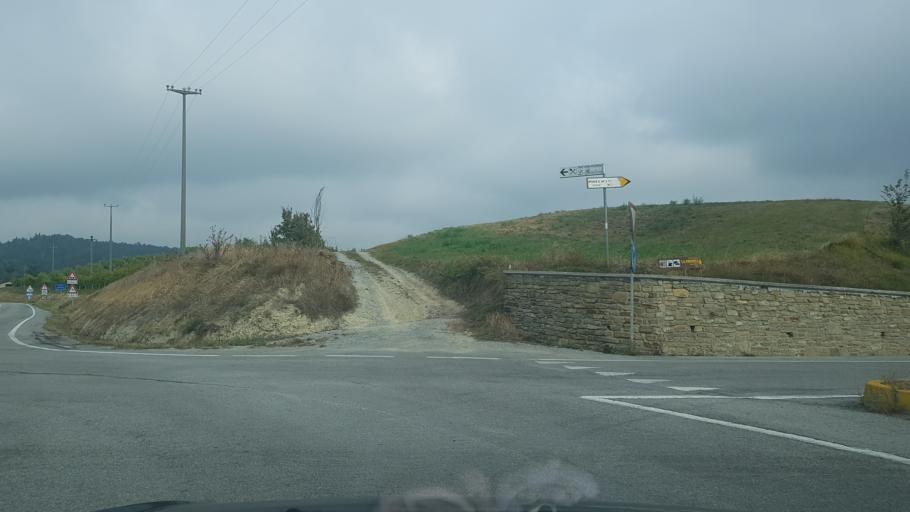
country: IT
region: Piedmont
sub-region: Provincia di Cuneo
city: Camerana
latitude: 44.4015
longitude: 8.1177
